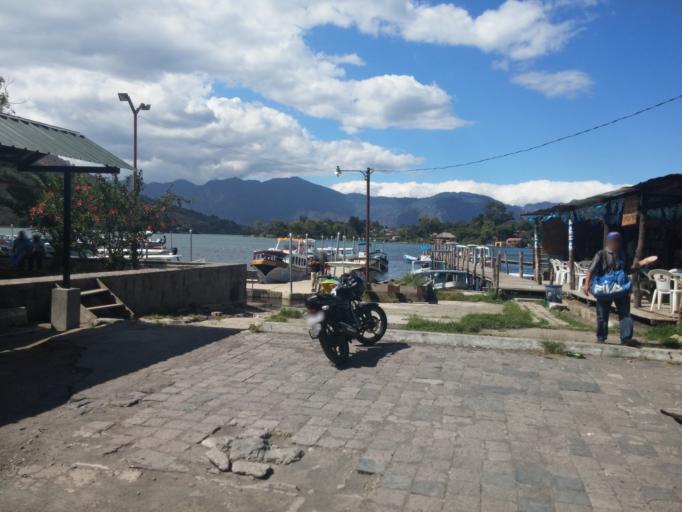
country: GT
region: Solola
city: Santiago Atitlan
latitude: 14.6427
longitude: -91.2295
